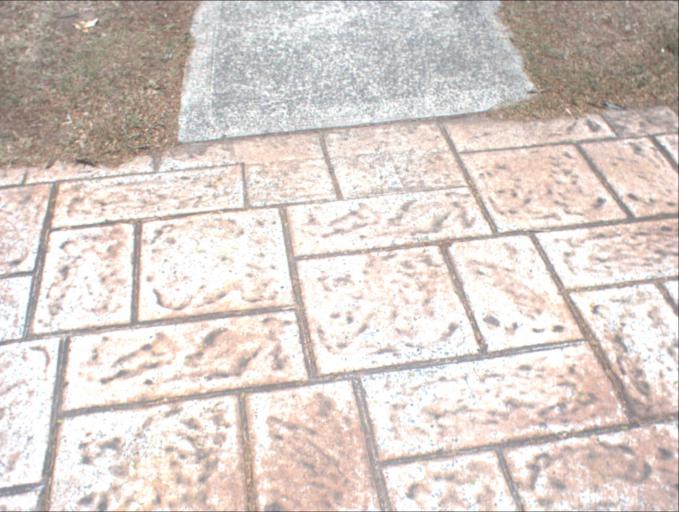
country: AU
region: Queensland
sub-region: Logan
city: Waterford West
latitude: -27.6987
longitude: 153.1664
